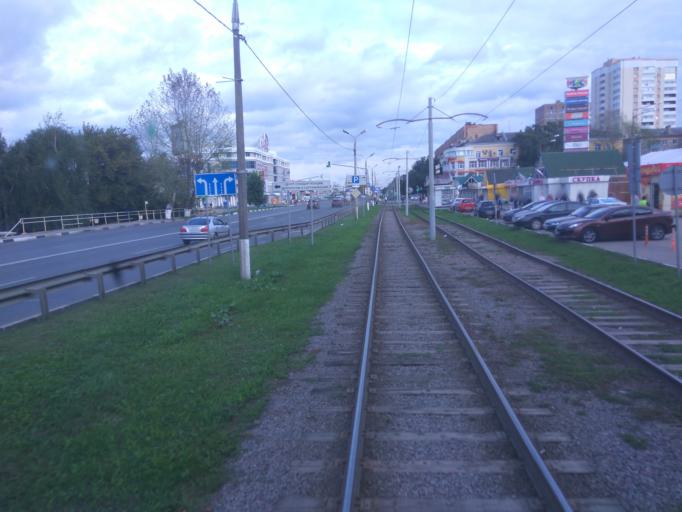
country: RU
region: Moskovskaya
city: Kolomna
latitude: 55.0845
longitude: 38.8013
